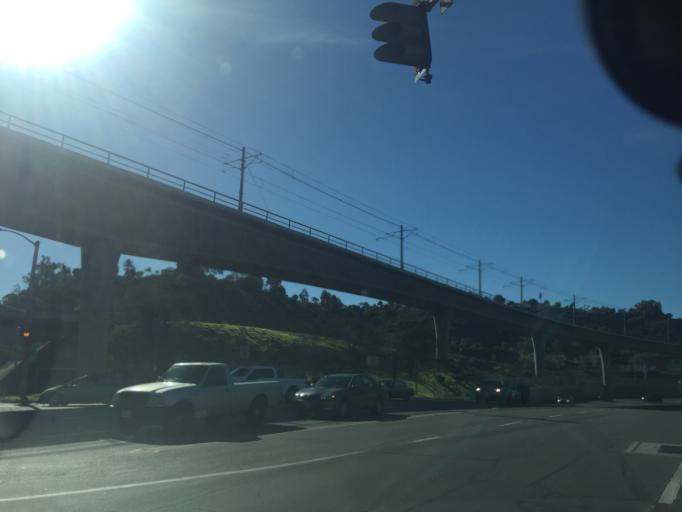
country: US
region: California
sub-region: San Diego County
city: La Mesa
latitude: 32.7803
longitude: -117.1017
